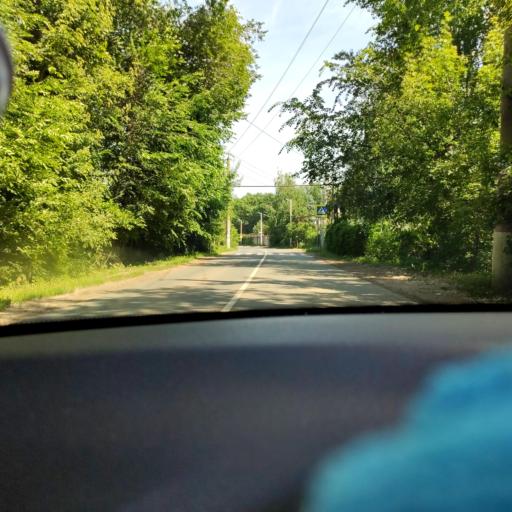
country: RU
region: Samara
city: Novokuybyshevsk
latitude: 53.1581
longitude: 49.9502
